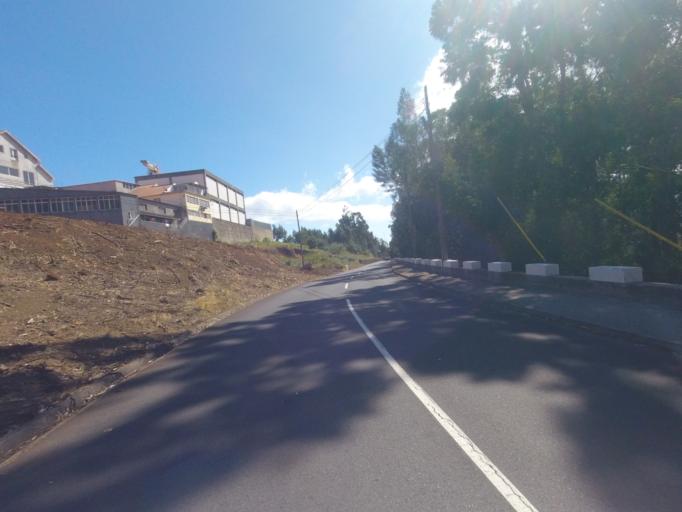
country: PT
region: Madeira
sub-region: Ribeira Brava
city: Campanario
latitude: 32.6844
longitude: -17.0404
